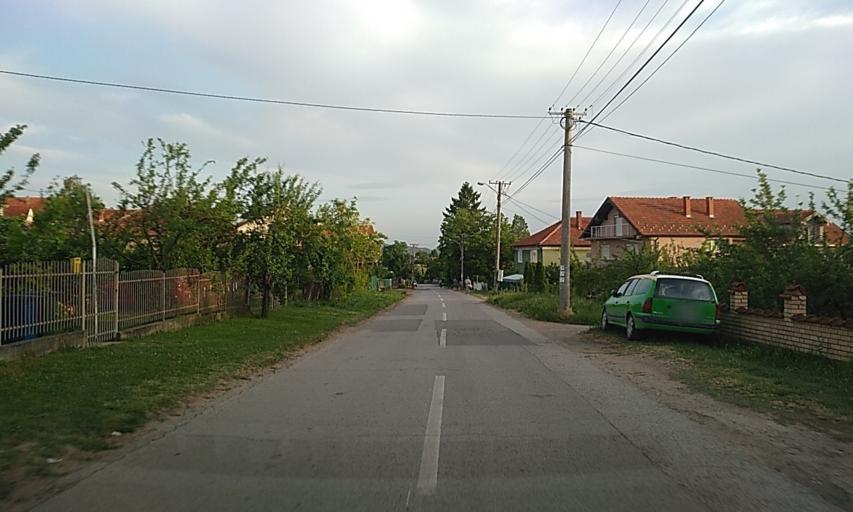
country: RS
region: Central Serbia
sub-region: Nisavski Okrug
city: Nis
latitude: 43.2968
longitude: 21.8662
